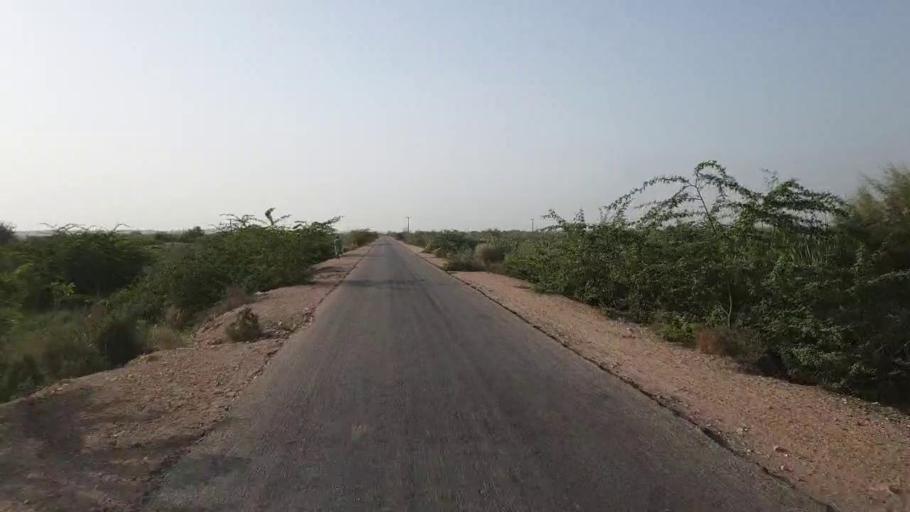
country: PK
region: Sindh
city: Jam Sahib
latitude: 26.4499
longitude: 68.8629
